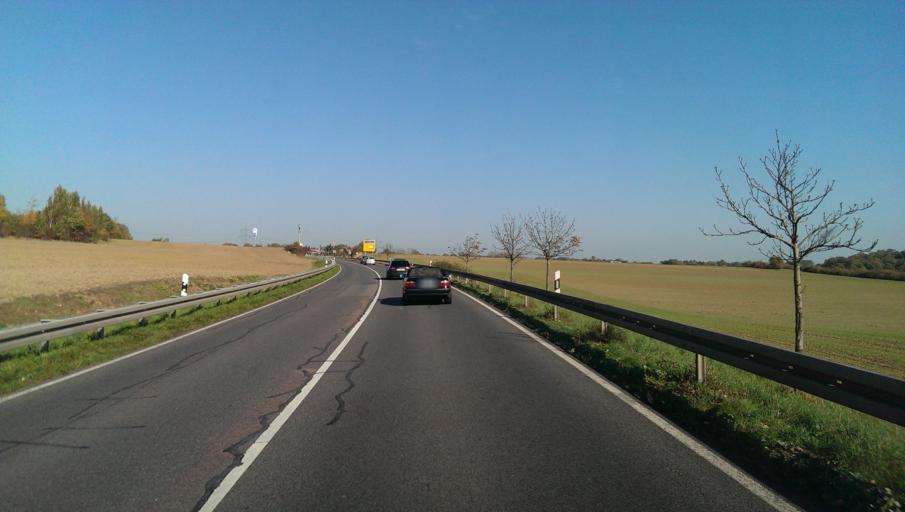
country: DE
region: Saxony
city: Dobeln
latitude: 51.1479
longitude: 13.1152
